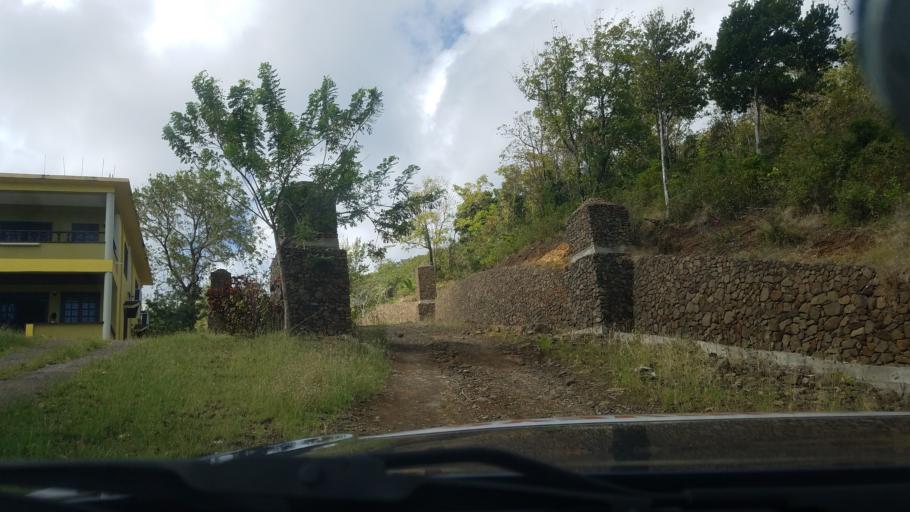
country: LC
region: Gros-Islet
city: Gros Islet
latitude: 14.0662
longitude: -60.9470
